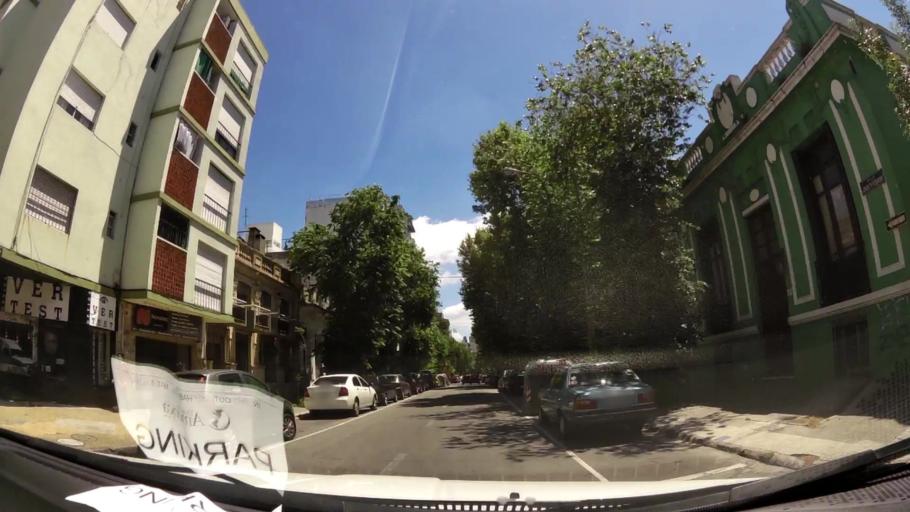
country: UY
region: Montevideo
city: Montevideo
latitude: -34.9039
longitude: -56.1689
